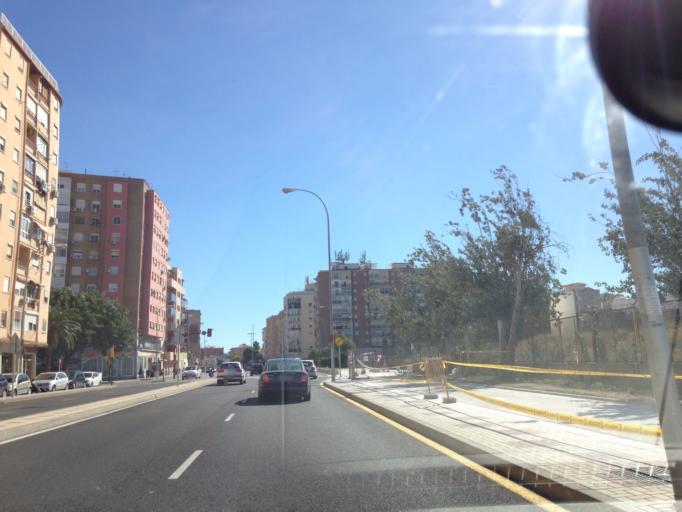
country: ES
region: Andalusia
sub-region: Provincia de Malaga
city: Malaga
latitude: 36.7056
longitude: -4.4421
